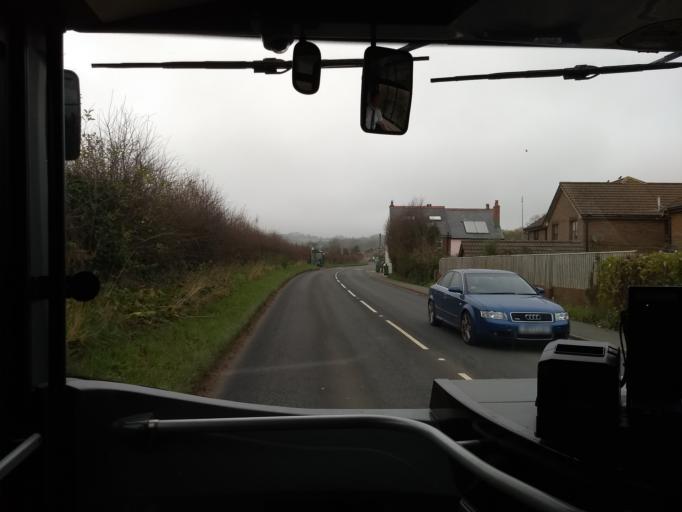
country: GB
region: England
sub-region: Isle of Wight
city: Newchurch
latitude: 50.6731
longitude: -1.2375
